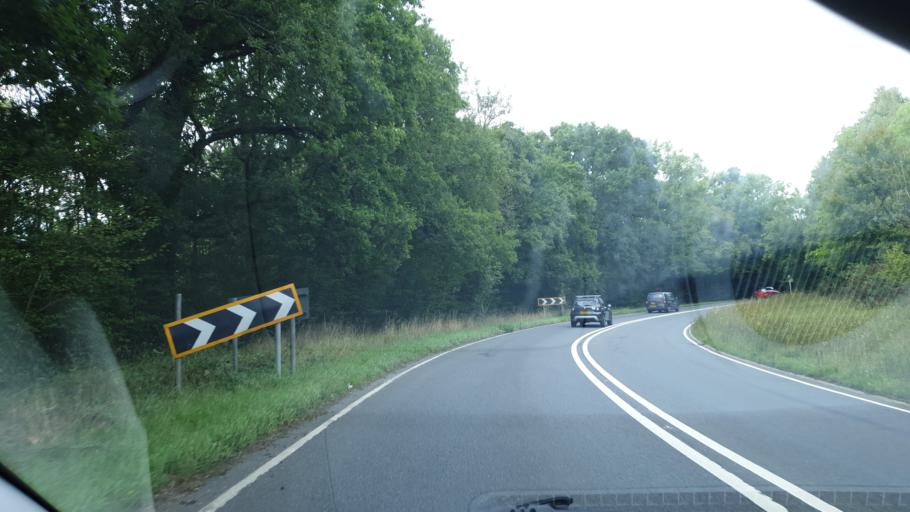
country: GB
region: England
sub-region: East Sussex
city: Forest Row
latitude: 51.1056
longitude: 0.0241
